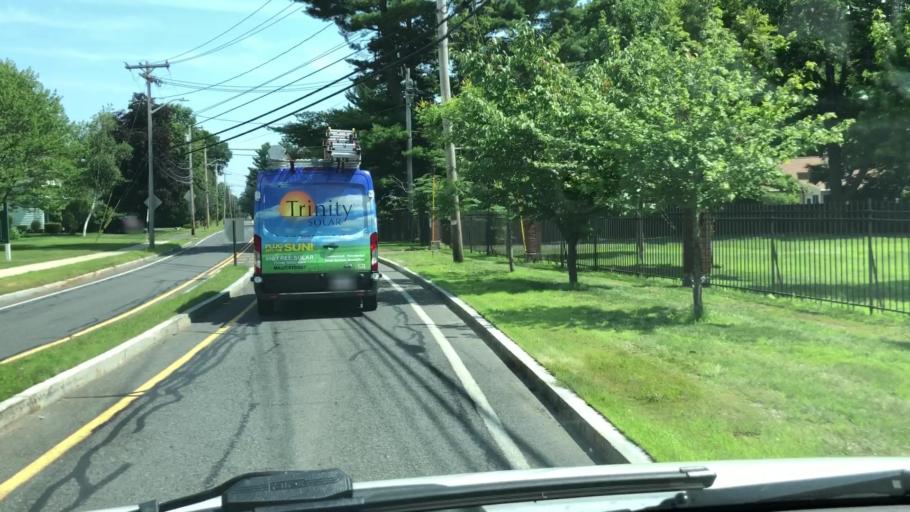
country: US
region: Massachusetts
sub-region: Hampshire County
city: Northampton
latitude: 42.3432
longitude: -72.6809
